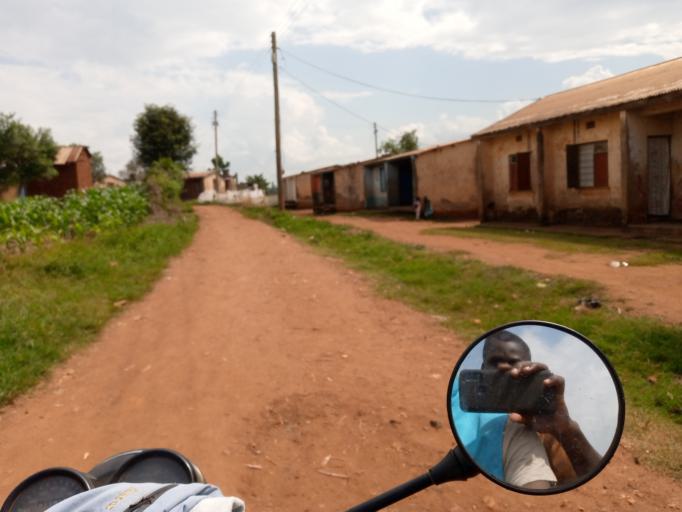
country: UG
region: Eastern Region
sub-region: Mbale District
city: Mbale
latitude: 1.0843
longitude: 34.1578
